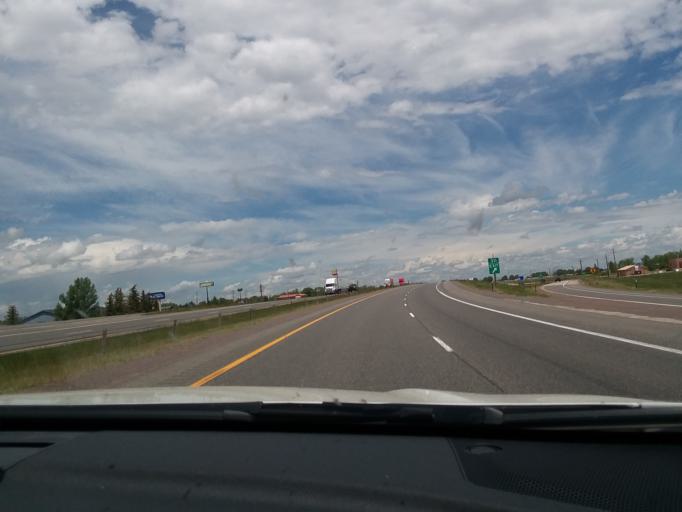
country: US
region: Wyoming
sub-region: Albany County
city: Laramie
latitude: 41.3053
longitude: -105.6137
